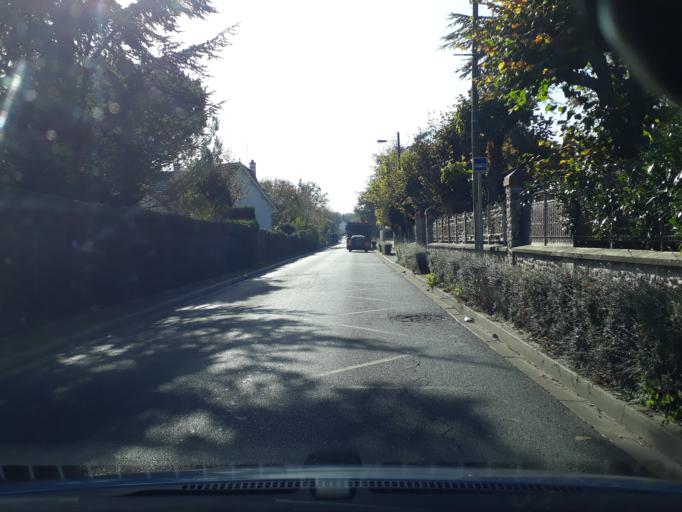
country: FR
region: Ile-de-France
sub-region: Departement de Seine-et-Marne
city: Bois-le-Roi
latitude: 48.4713
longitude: 2.6920
